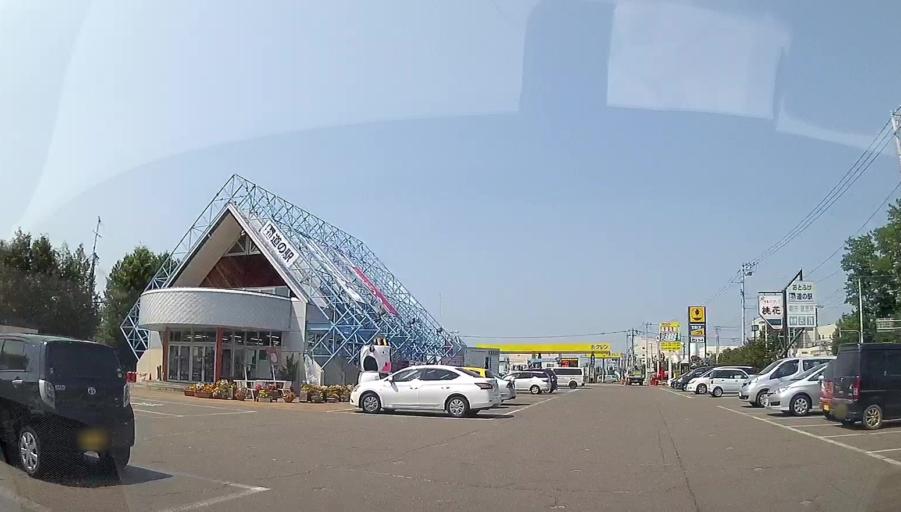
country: JP
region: Hokkaido
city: Otofuke
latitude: 42.9764
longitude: 143.2077
